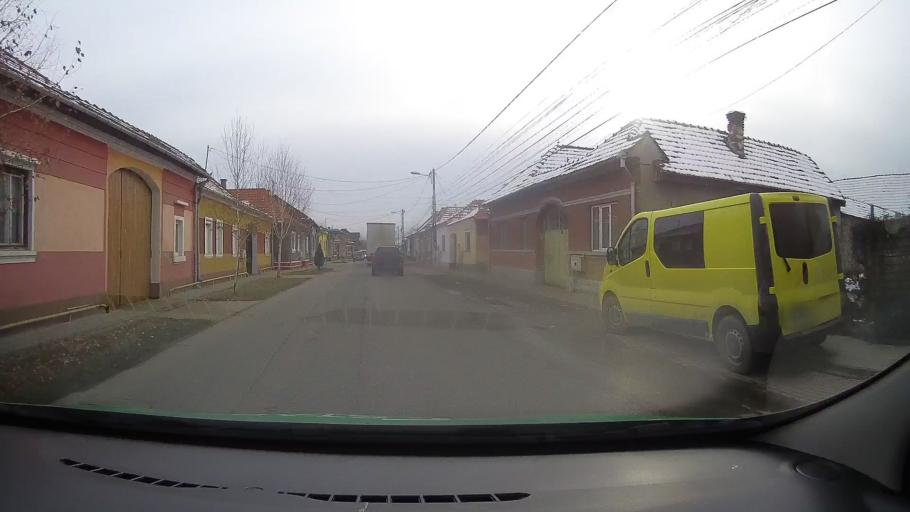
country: RO
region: Hunedoara
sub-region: Comuna Geoagiu
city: Geoagiu
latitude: 45.9037
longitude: 23.2231
